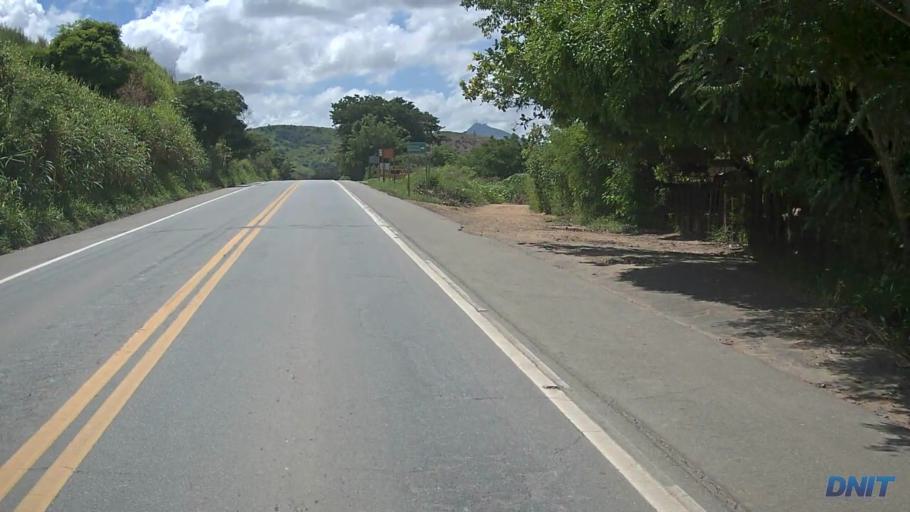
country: BR
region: Minas Gerais
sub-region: Governador Valadares
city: Governador Valadares
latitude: -18.9297
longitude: -42.0444
